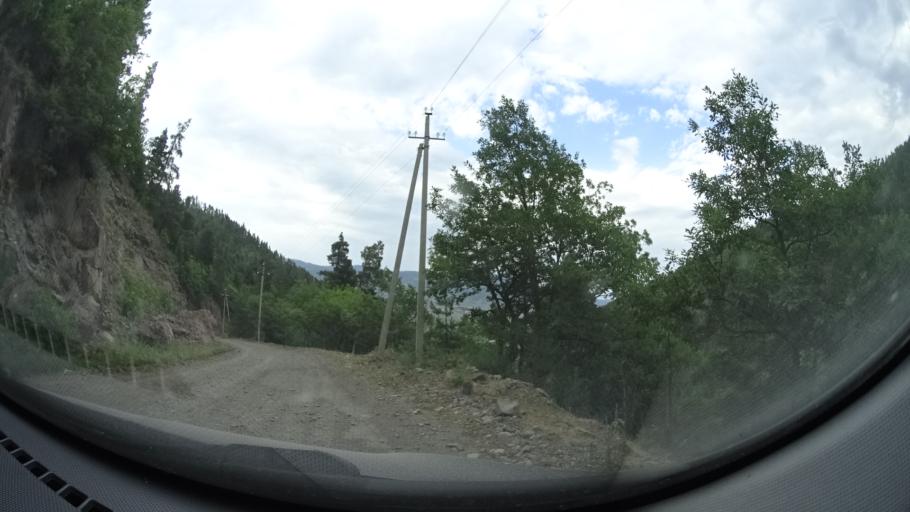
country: GE
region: Samtskhe-Javakheti
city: Adigeni
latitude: 41.6732
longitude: 42.6398
